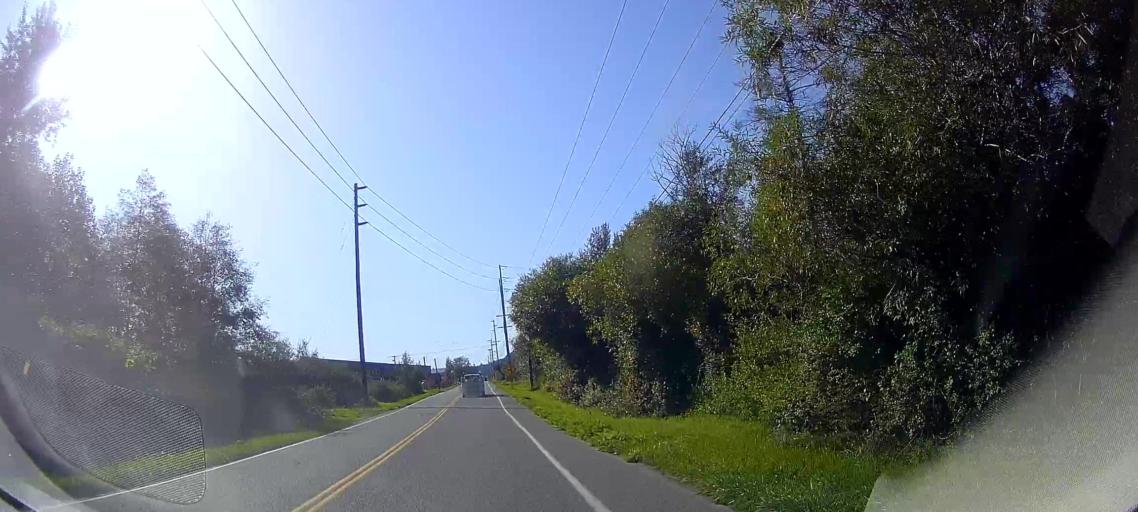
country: US
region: Washington
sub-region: Skagit County
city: Anacortes
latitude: 48.4649
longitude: -122.5411
